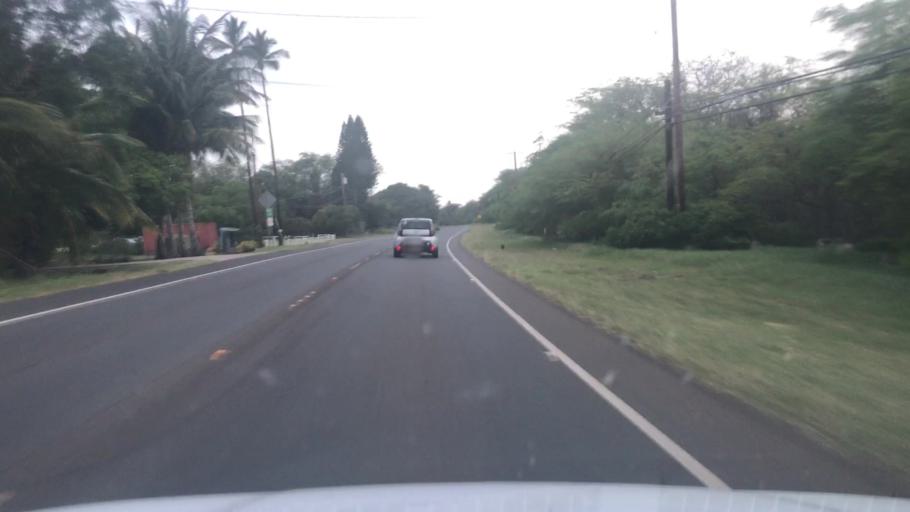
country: US
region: Hawaii
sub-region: Maui County
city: Kaunakakai
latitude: 21.0674
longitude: -156.9573
